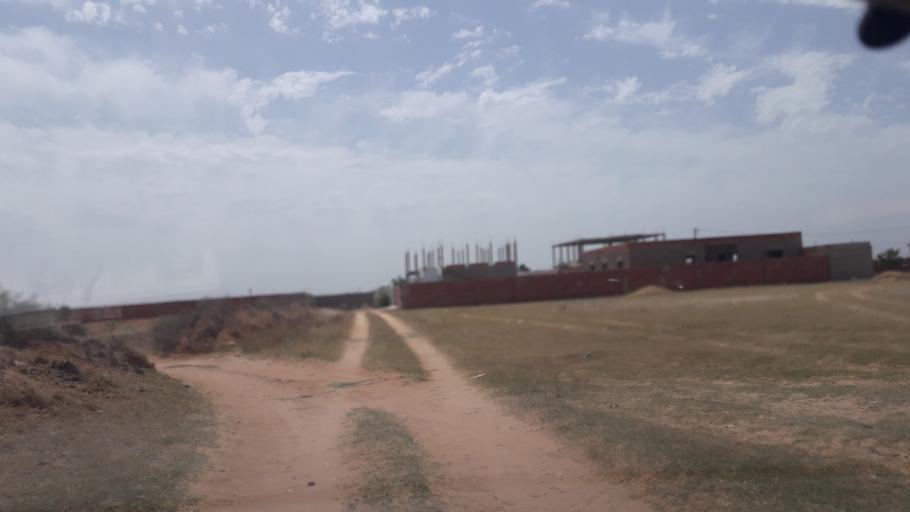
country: TN
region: Safaqis
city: Al Qarmadah
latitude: 34.8362
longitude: 10.7701
